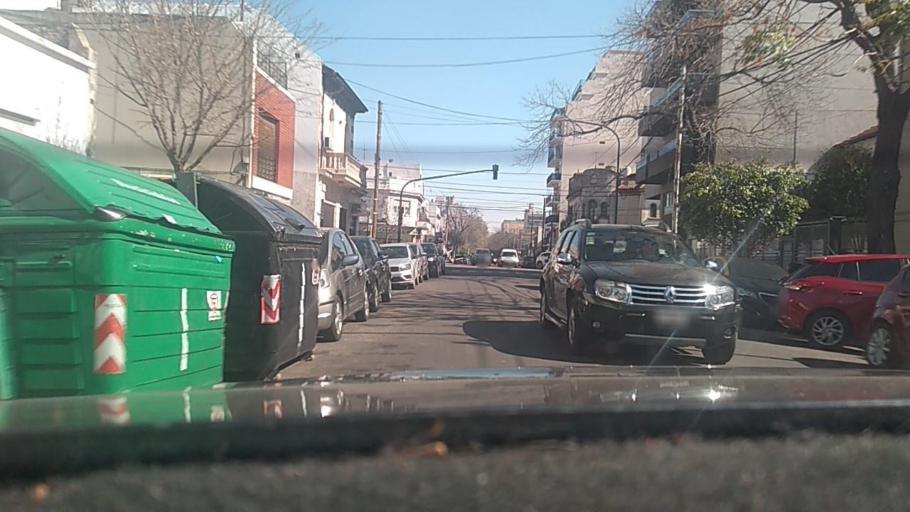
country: AR
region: Buenos Aires F.D.
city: Villa Santa Rita
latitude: -34.6032
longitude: -58.4877
